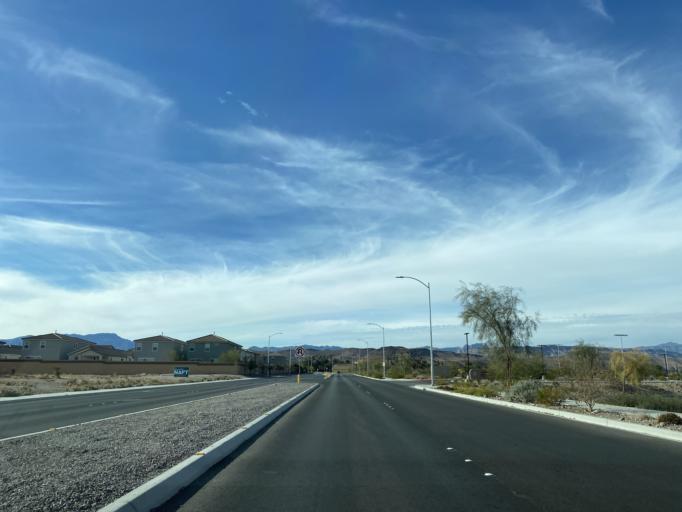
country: US
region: Nevada
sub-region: Clark County
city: Enterprise
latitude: 36.0482
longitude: -115.2734
